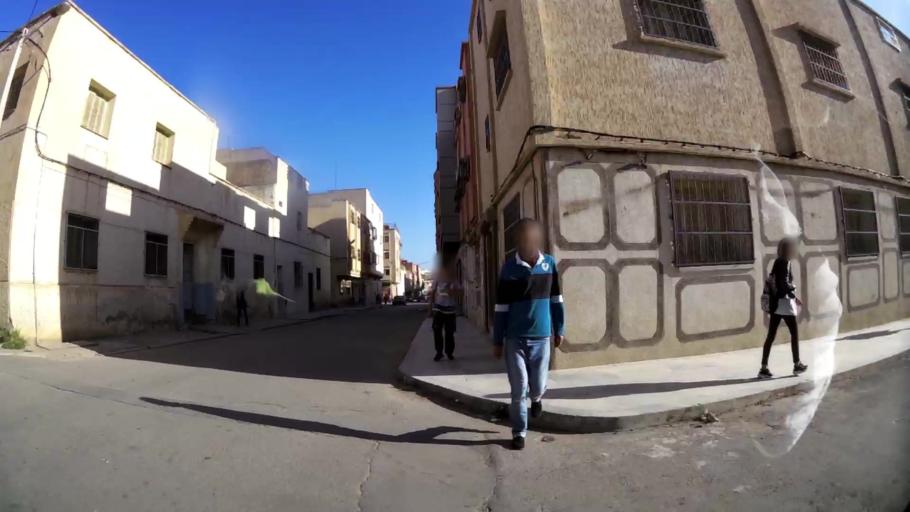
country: MA
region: Oriental
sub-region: Oujda-Angad
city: Oujda
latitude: 34.6931
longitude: -1.9162
